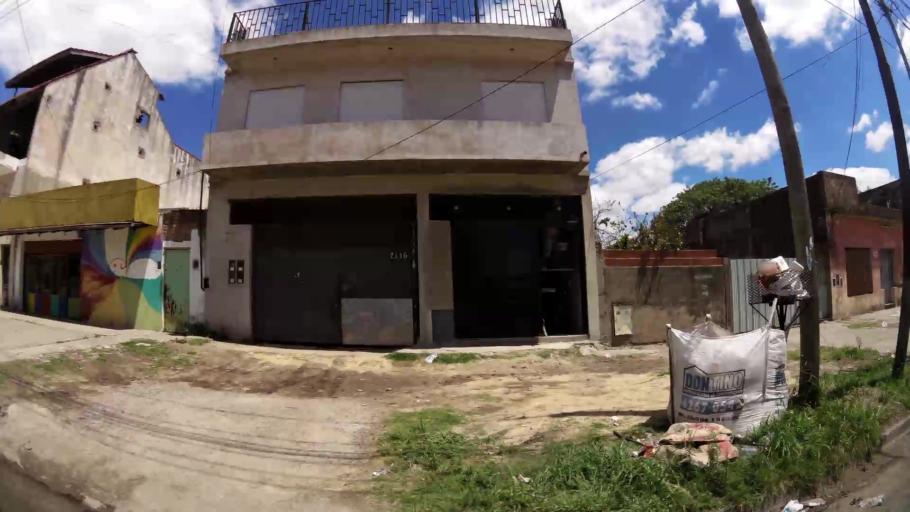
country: AR
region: Buenos Aires
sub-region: Partido de Lanus
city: Lanus
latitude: -34.7176
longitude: -58.4133
